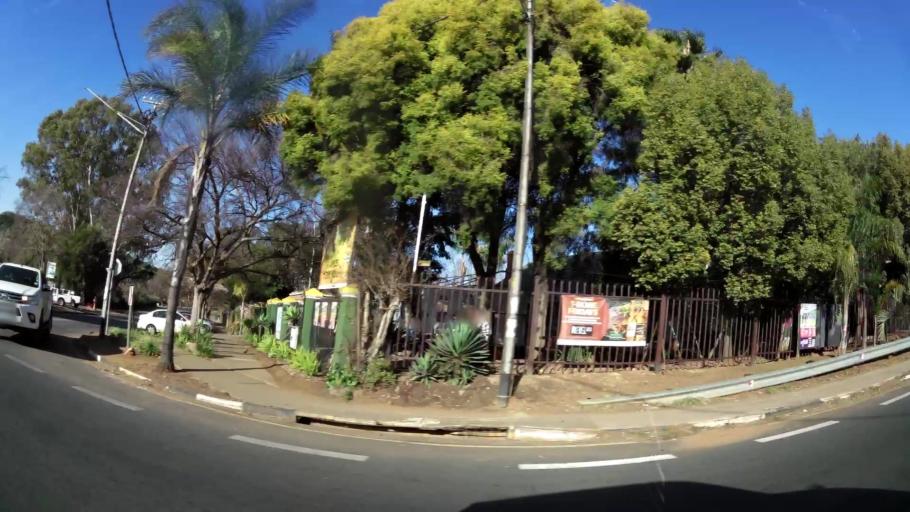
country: ZA
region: Gauteng
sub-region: City of Tshwane Metropolitan Municipality
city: Pretoria
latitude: -25.7295
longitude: 28.2152
